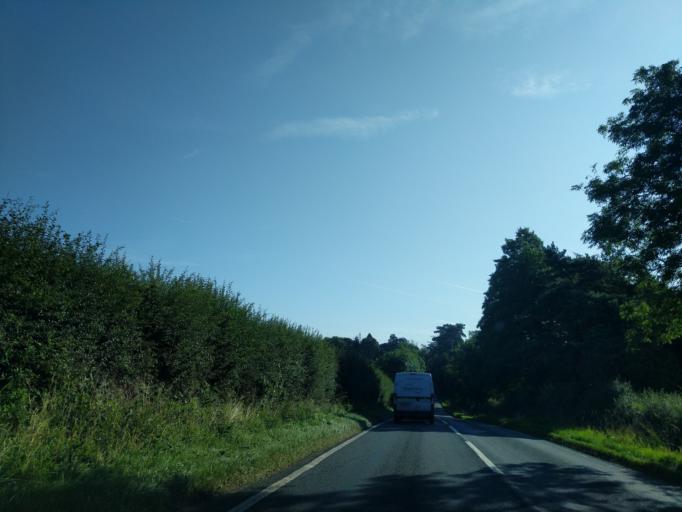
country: GB
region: England
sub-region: District of Rutland
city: Clipsham
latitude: 52.8005
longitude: -0.5595
